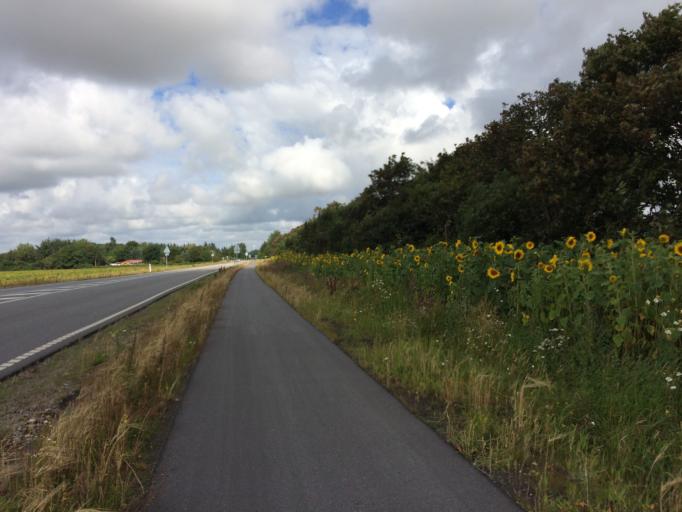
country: DK
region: Central Jutland
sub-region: Holstebro Kommune
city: Ulfborg
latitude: 56.3275
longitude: 8.3436
